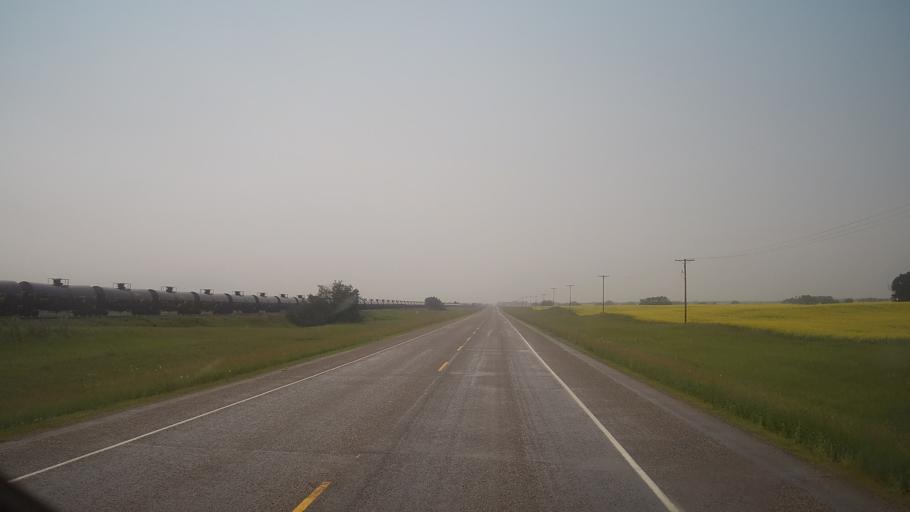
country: CA
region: Saskatchewan
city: Biggar
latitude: 52.1587
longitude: -108.2695
